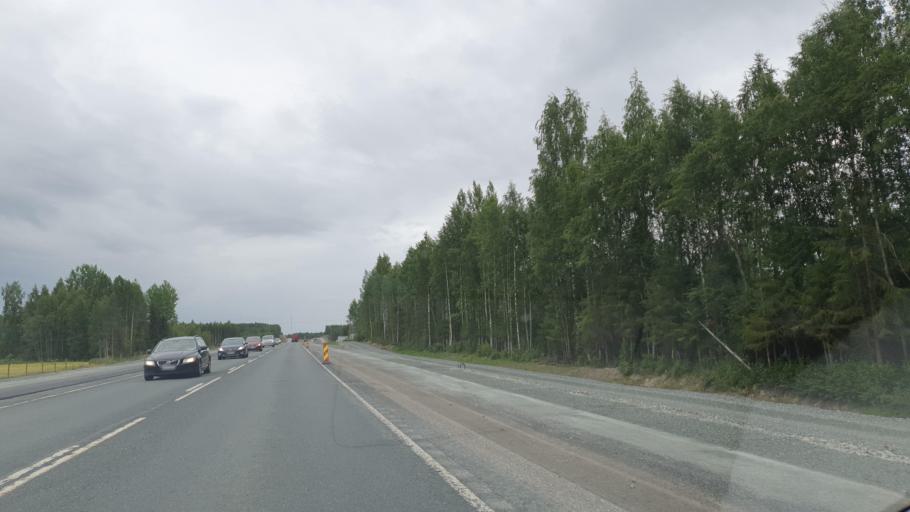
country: FI
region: Northern Savo
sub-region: Ylae-Savo
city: Lapinlahti
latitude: 63.2941
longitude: 27.4533
